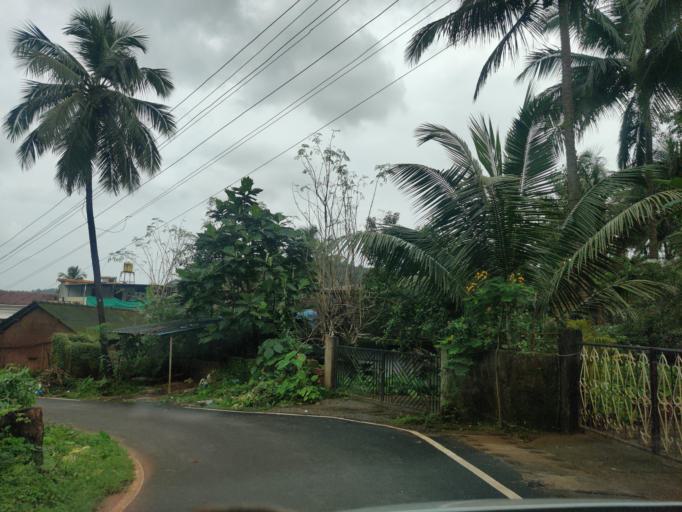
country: IN
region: Goa
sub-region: North Goa
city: Valpoy
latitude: 15.5270
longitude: 74.1417
